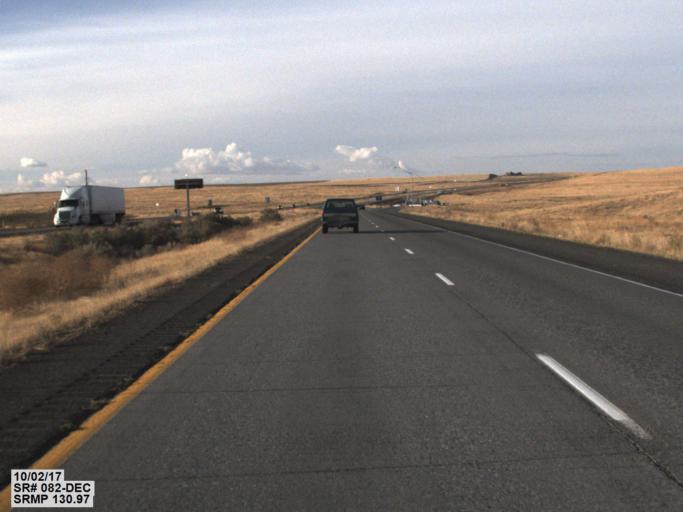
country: US
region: Oregon
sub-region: Umatilla County
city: Umatilla
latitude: 45.9540
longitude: -119.3391
